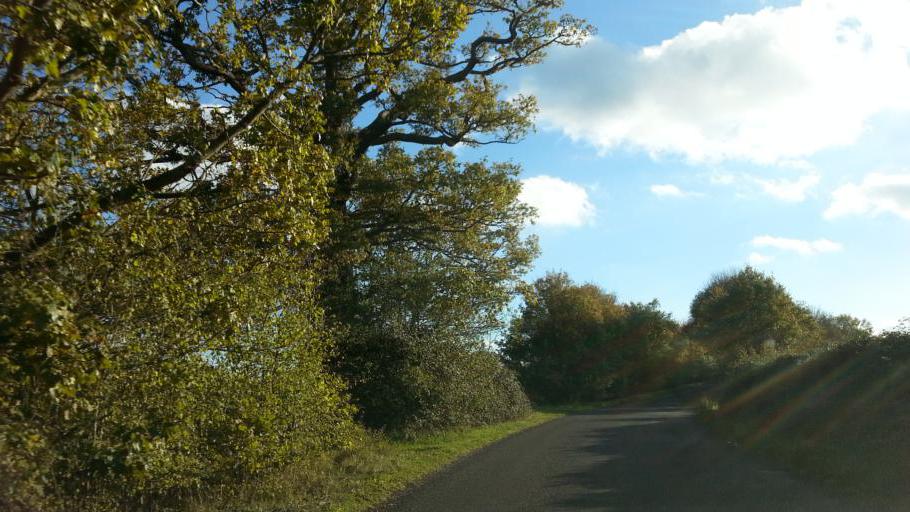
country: GB
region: England
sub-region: Suffolk
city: Thurston
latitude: 52.2381
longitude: 0.8080
